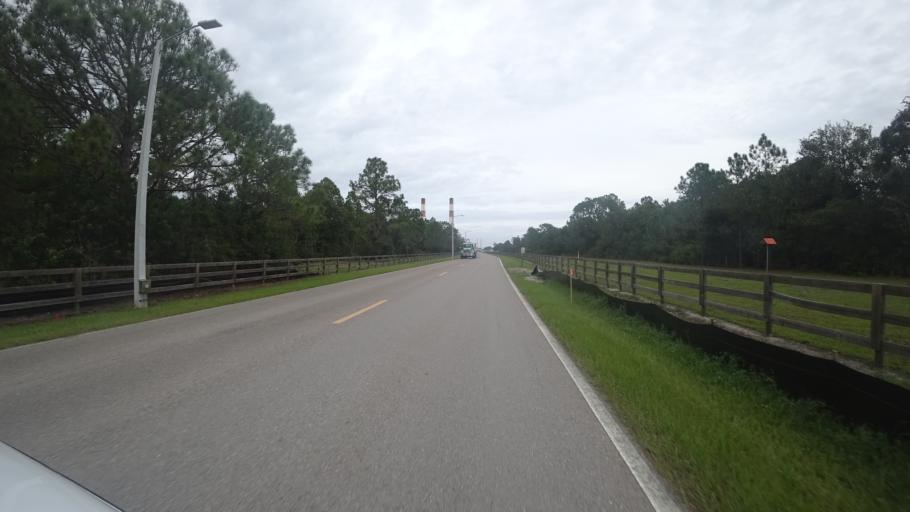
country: US
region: Florida
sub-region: Hillsborough County
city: Sun City Center
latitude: 27.5970
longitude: -82.3441
